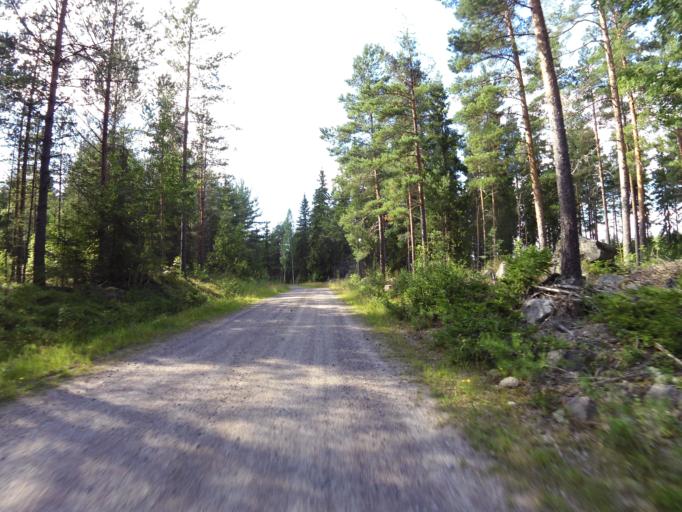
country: SE
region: Dalarna
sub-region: Faluns Kommun
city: Svardsjo
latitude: 60.6908
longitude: 15.8986
